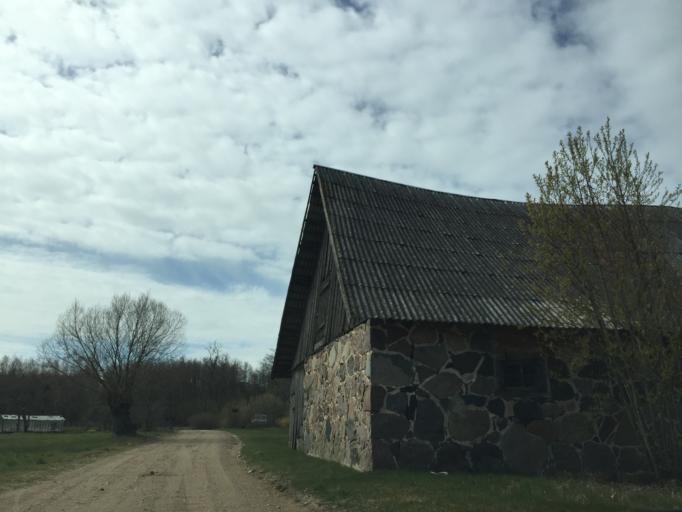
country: LV
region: Salacgrivas
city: Salacgriva
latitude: 57.5895
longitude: 24.3718
